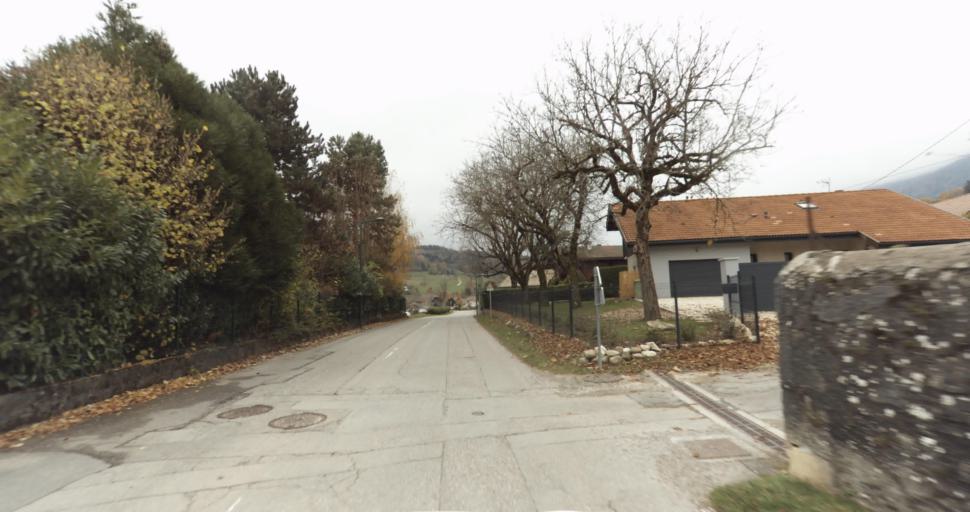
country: FR
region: Rhone-Alpes
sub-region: Departement de la Haute-Savoie
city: Saint-Jorioz
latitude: 45.8301
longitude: 6.1516
